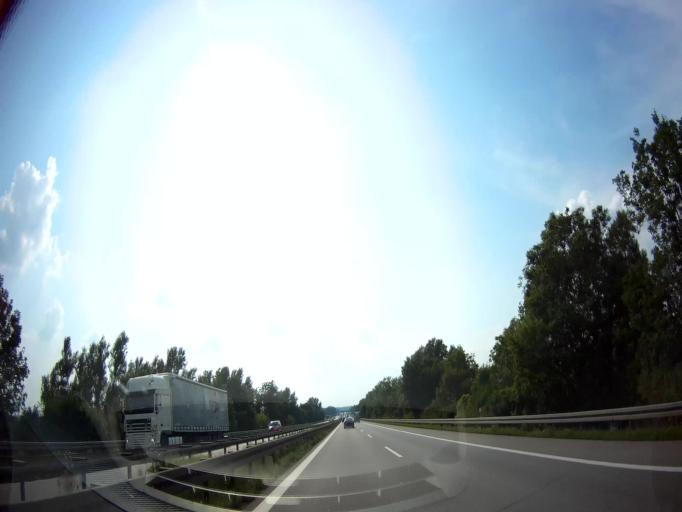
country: DE
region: Bavaria
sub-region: Upper Palatinate
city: Wiesent
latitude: 48.9957
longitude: 12.3322
